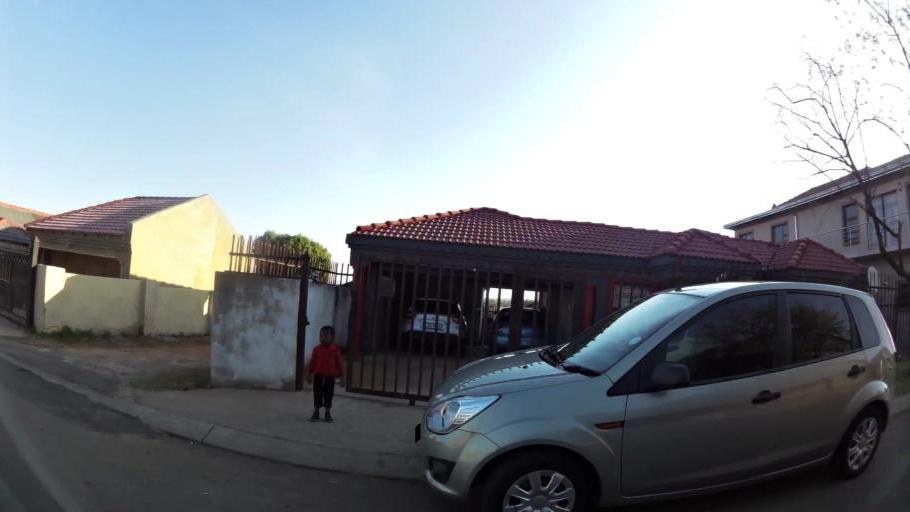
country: ZA
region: Gauteng
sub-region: City of Tshwane Metropolitan Municipality
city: Pretoria
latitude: -25.7341
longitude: 28.1186
